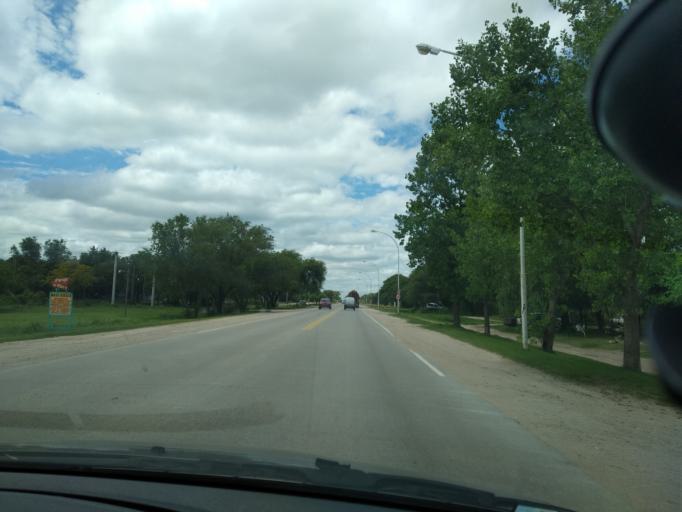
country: AR
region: Cordoba
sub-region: Departamento de Rio Segundo
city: Rio Segundo
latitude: -31.6454
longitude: -63.9025
